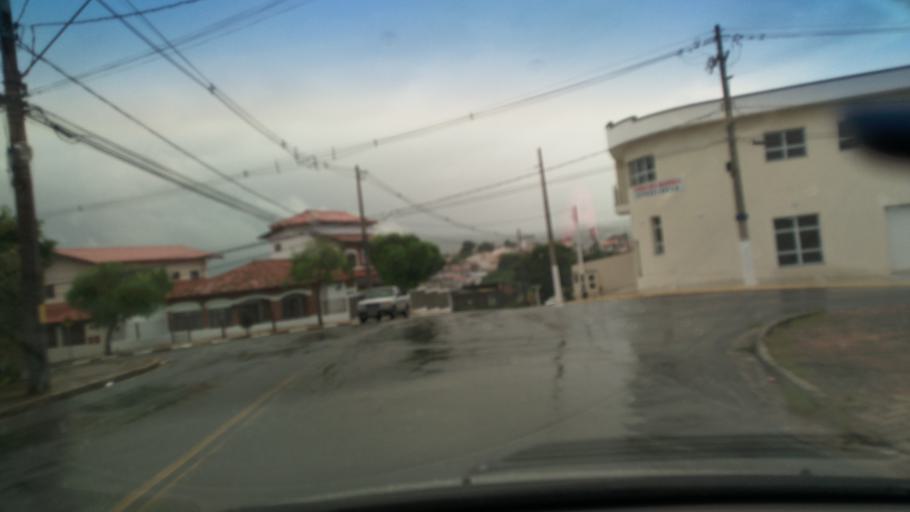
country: BR
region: Sao Paulo
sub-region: Valinhos
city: Valinhos
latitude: -22.9554
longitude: -46.9994
